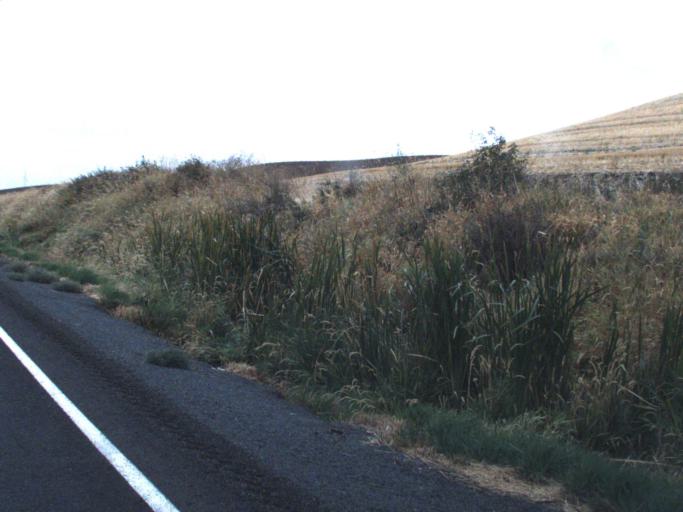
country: US
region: Washington
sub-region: Whitman County
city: Colfax
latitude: 47.1755
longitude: -117.2924
